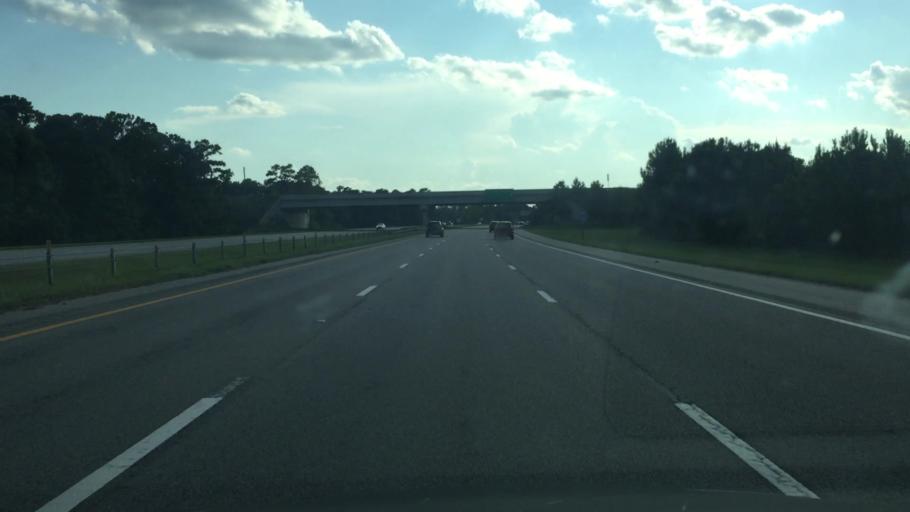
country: US
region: South Carolina
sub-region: Horry County
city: Myrtle Beach
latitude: 33.7549
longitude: -78.8506
